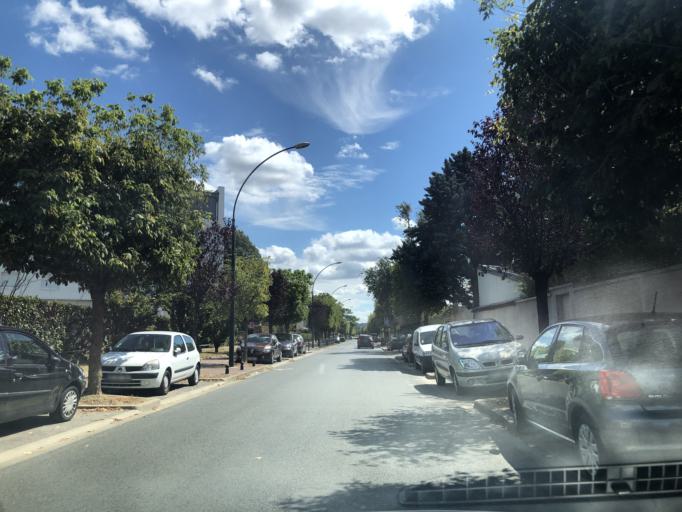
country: FR
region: Ile-de-France
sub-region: Departement du Val-de-Marne
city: Saint-Maur-des-Fosses
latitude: 48.7971
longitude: 2.4924
